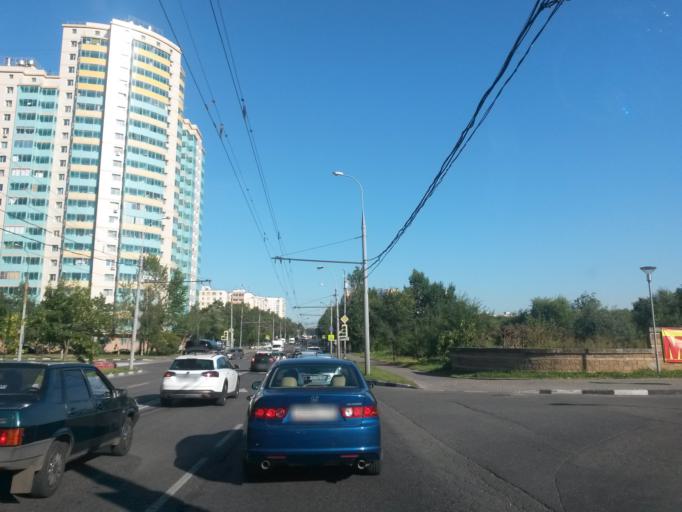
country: RU
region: Moscow
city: Yasenevo
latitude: 55.5984
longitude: 37.5283
